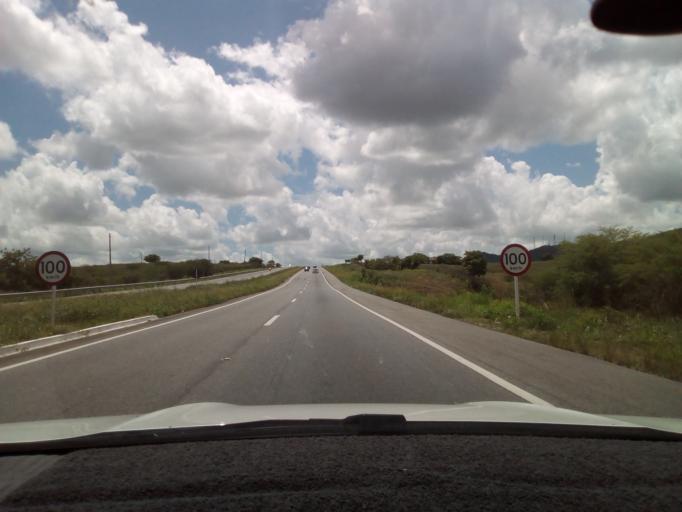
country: BR
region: Paraiba
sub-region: Gurinhem
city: Gurinhem
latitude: -7.1841
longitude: -35.4424
